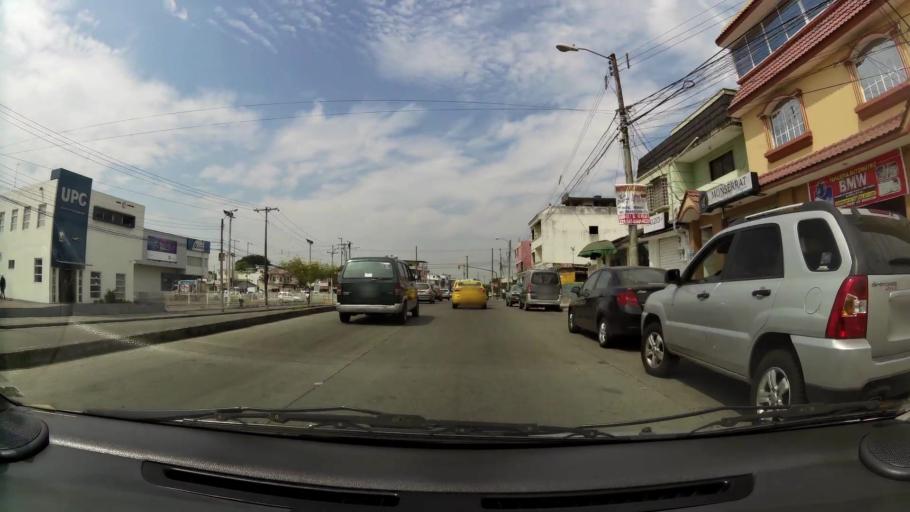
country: EC
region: Guayas
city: Eloy Alfaro
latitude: -2.1210
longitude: -79.9012
